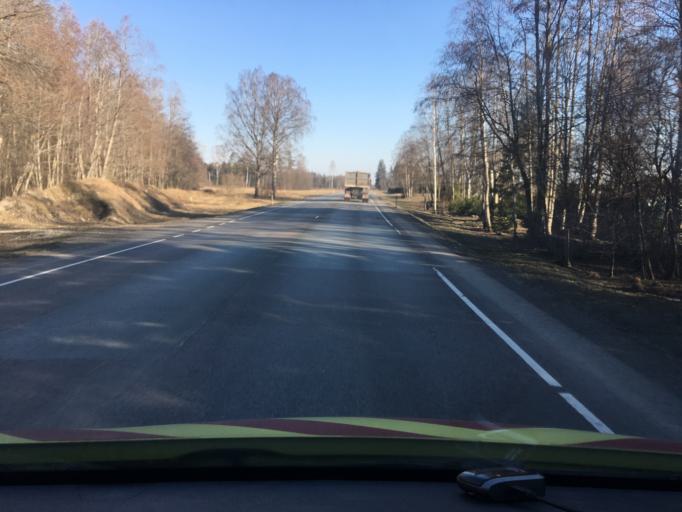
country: EE
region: Raplamaa
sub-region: Kohila vald
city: Kohila
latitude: 59.2569
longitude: 24.7410
